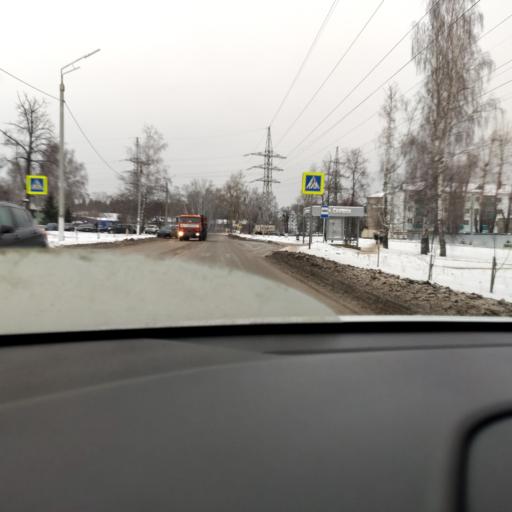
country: RU
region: Tatarstan
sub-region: Zelenodol'skiy Rayon
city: Zelenodolsk
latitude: 55.8539
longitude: 48.4922
